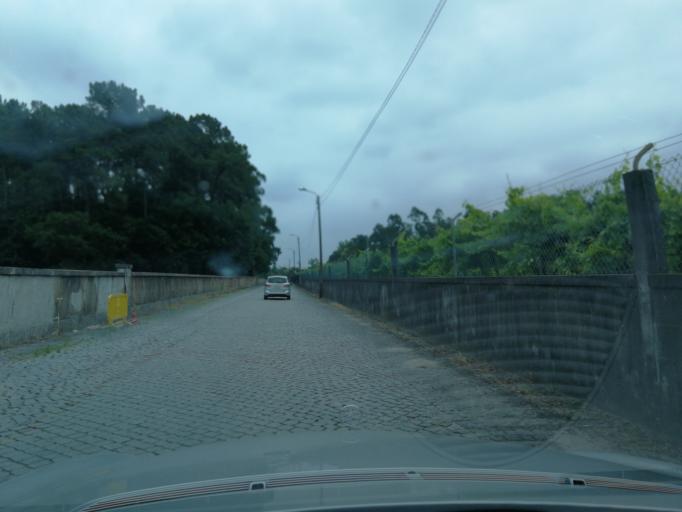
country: PT
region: Braga
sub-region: Vila Verde
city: Prado
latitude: 41.6009
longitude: -8.4438
